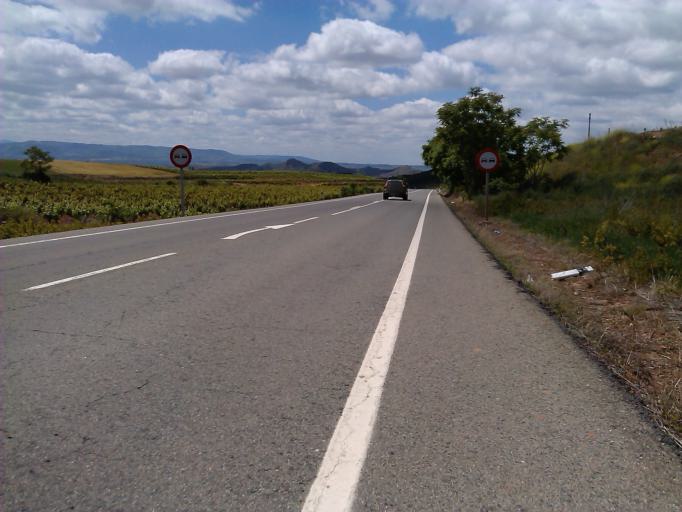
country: ES
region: La Rioja
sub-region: Provincia de La Rioja
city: Aleson
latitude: 42.4117
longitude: -2.6699
